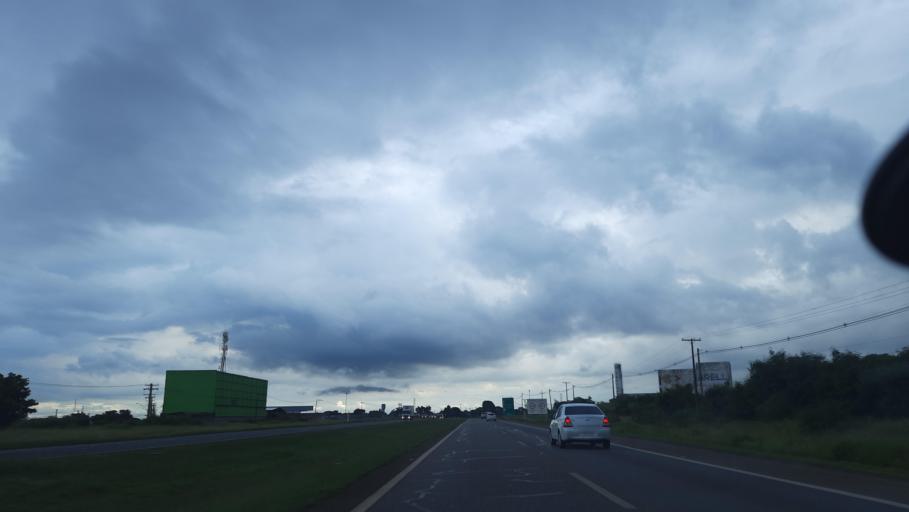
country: BR
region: Sao Paulo
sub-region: Moji-Guacu
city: Mogi-Gaucu
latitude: -22.3420
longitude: -46.9574
